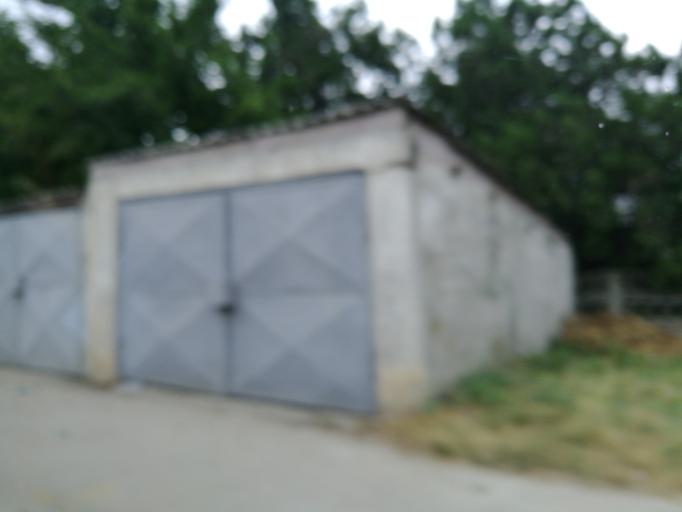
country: RO
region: Constanta
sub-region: Municipiul Mangalia
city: Mangalia
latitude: 43.8147
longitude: 28.5727
